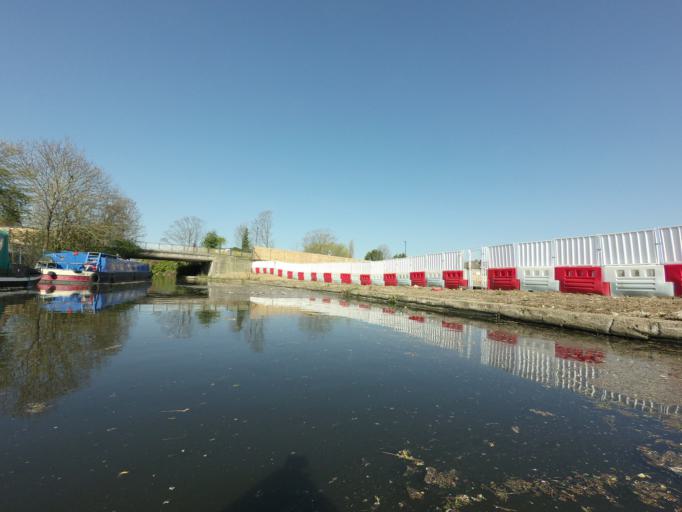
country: GB
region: England
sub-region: Greater London
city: Greenford
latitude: 51.5479
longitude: -0.3435
